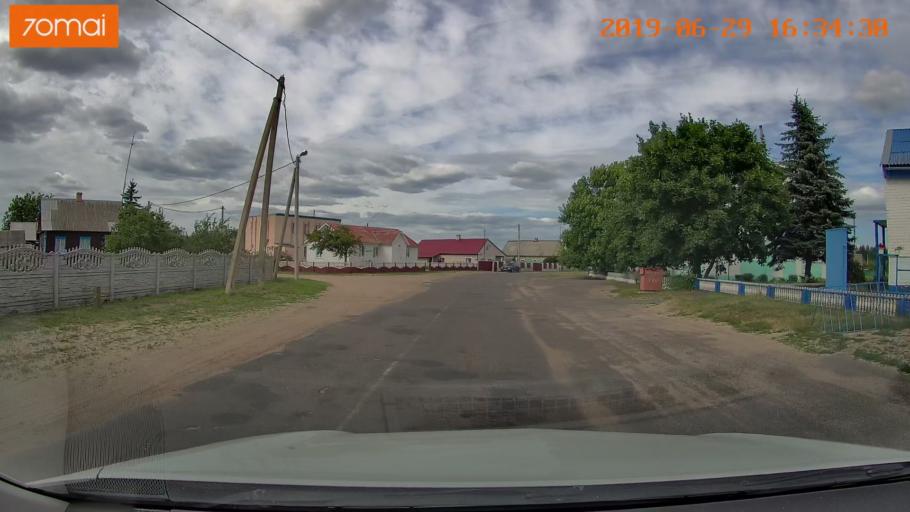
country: BY
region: Brest
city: Luninyets
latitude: 52.2069
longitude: 27.0103
